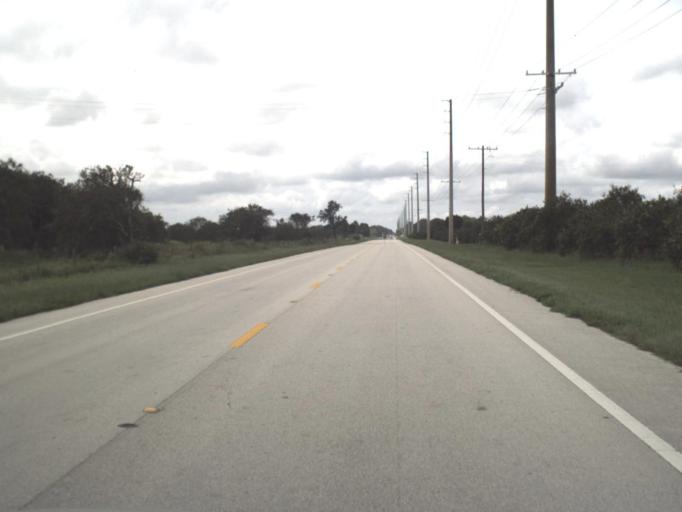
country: US
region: Florida
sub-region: Hardee County
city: Bowling Green
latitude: 27.5949
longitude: -81.9516
